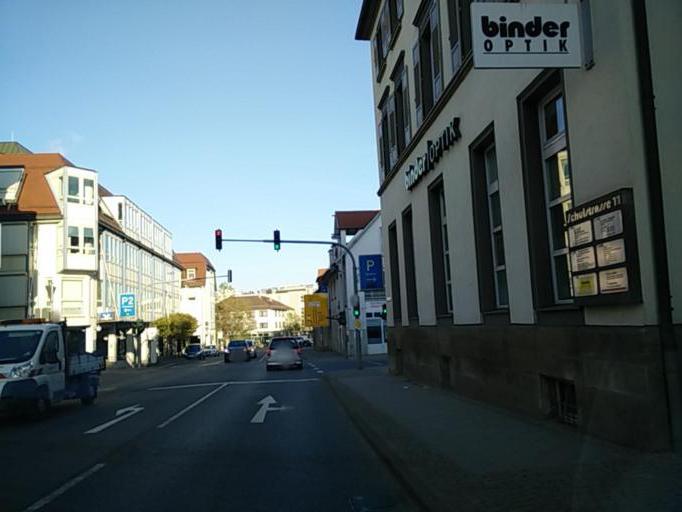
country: DE
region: Baden-Wuerttemberg
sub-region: Regierungsbezirk Stuttgart
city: Herrenberg
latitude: 48.5948
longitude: 8.8699
